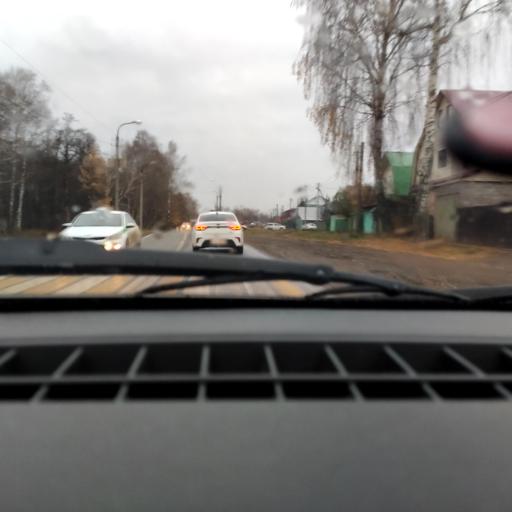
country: RU
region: Bashkortostan
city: Ufa
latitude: 54.8141
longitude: 56.1638
